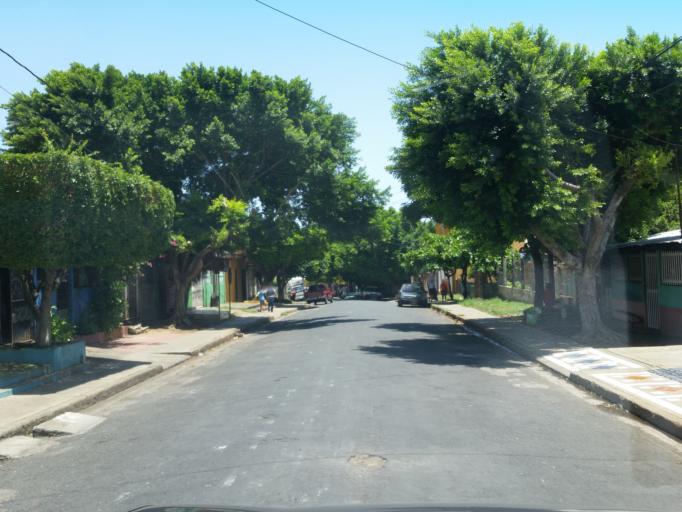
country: NI
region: Managua
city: Managua
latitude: 12.1174
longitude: -86.2372
